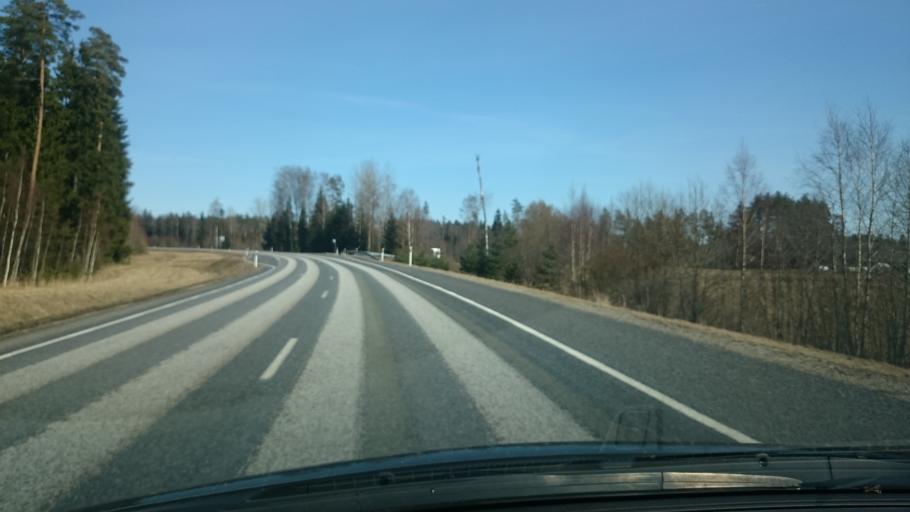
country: EE
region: Jaervamaa
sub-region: Tueri vald
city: Sarevere
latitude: 58.7343
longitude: 25.2959
